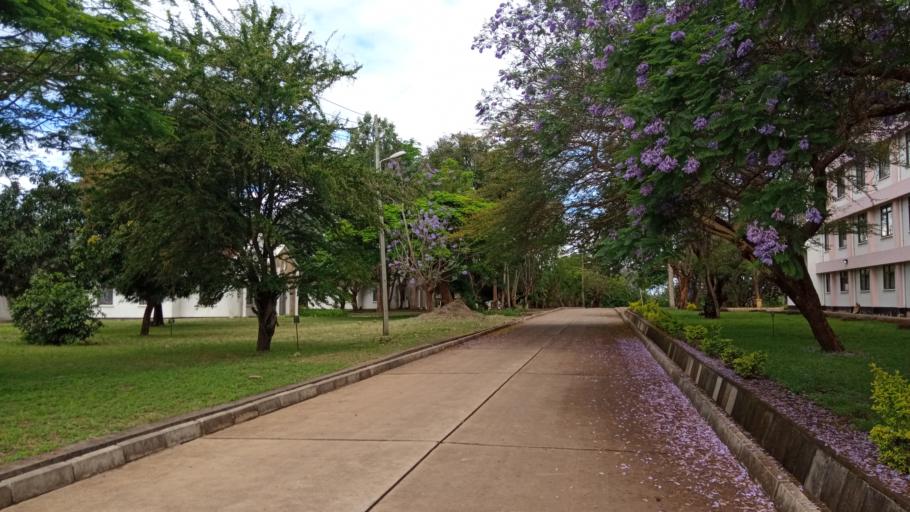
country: TZ
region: Arusha
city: Usa River
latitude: -3.3986
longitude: 36.7991
